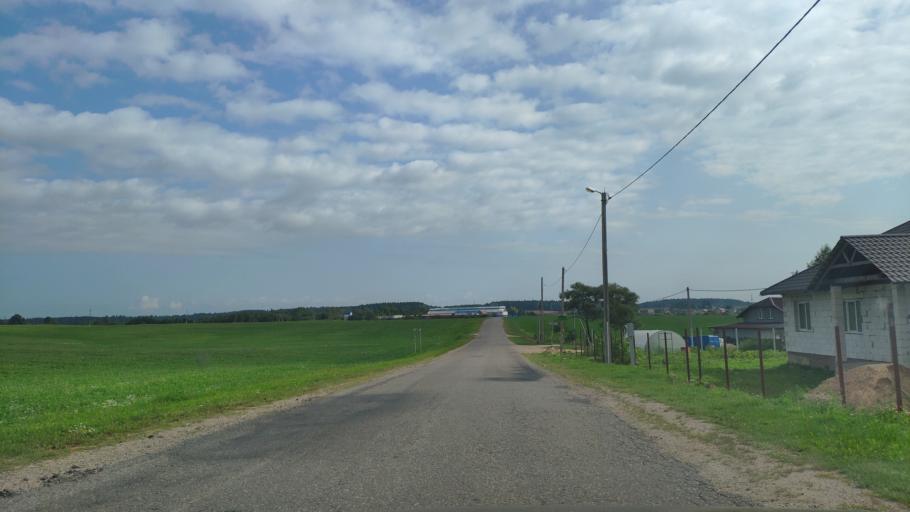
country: BY
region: Minsk
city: Khatsyezhyna
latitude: 53.8574
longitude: 27.3076
